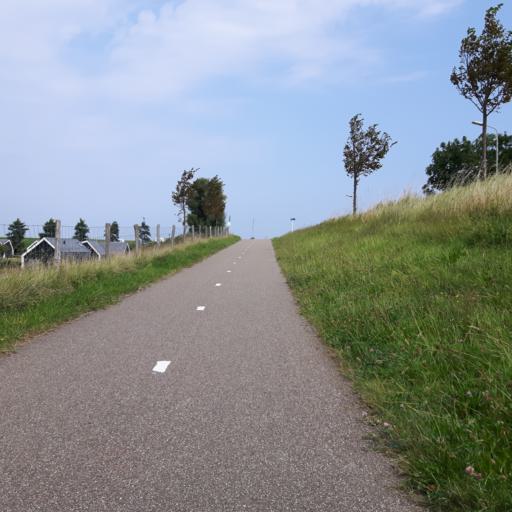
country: NL
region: Zeeland
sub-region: Gemeente Goes
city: Goes
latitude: 51.5235
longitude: 3.9393
